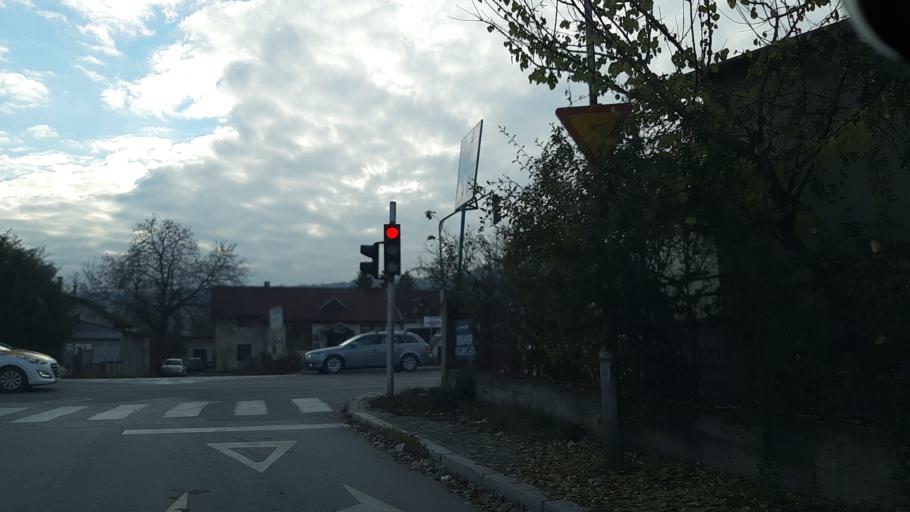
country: MK
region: Kisela Voda
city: Usje
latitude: 41.9744
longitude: 21.4560
